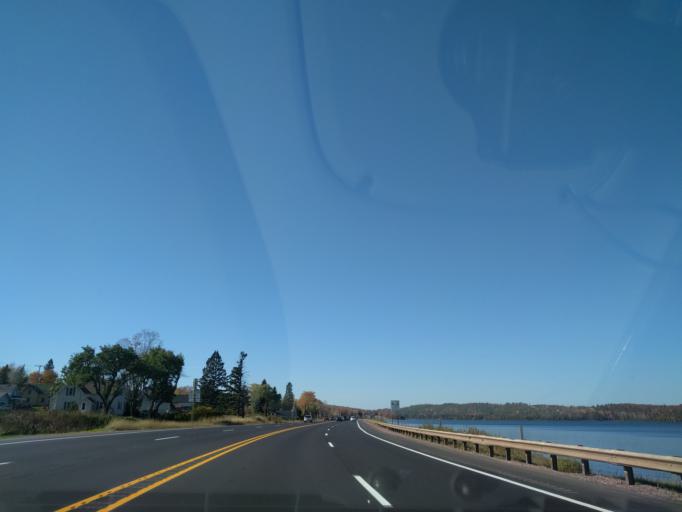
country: US
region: Michigan
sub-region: Marquette County
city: Negaunee
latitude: 46.5066
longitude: -87.6148
